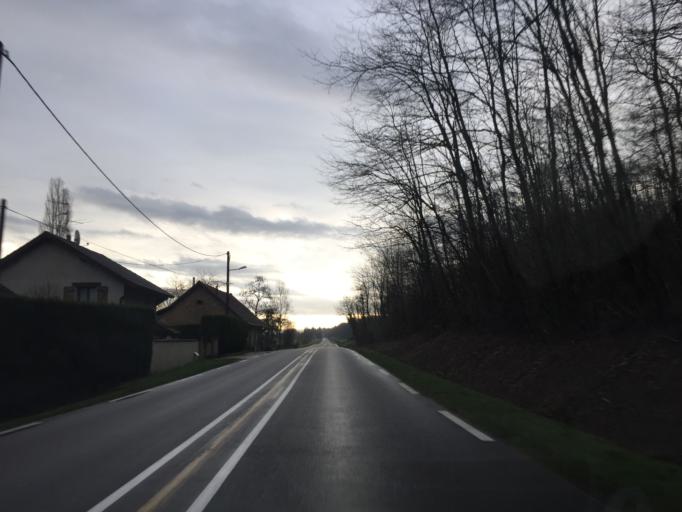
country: FR
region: Franche-Comte
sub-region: Departement du Jura
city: Mont-sous-Vaudrey
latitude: 47.0013
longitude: 5.5292
